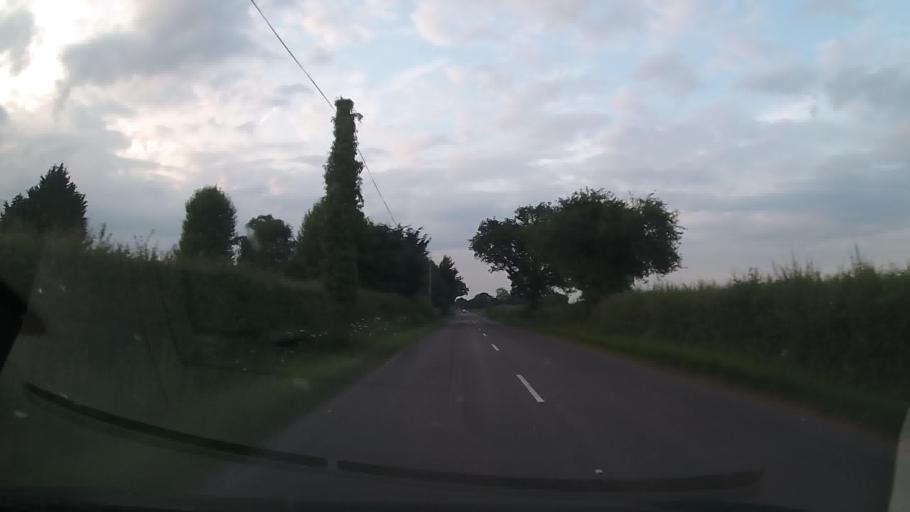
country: GB
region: England
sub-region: Shropshire
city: Wem
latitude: 52.8380
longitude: -2.7314
